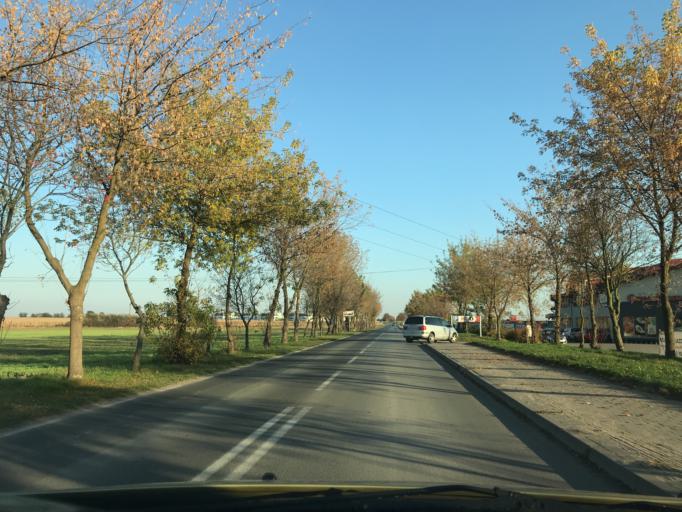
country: PL
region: Greater Poland Voivodeship
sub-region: Powiat poznanski
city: Baranowo
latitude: 52.3975
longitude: 16.7562
